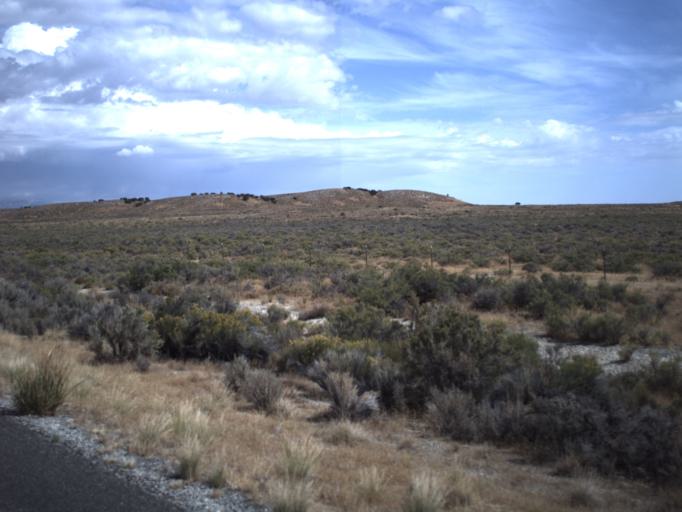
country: US
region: Idaho
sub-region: Cassia County
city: Burley
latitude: 41.6732
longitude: -113.5433
